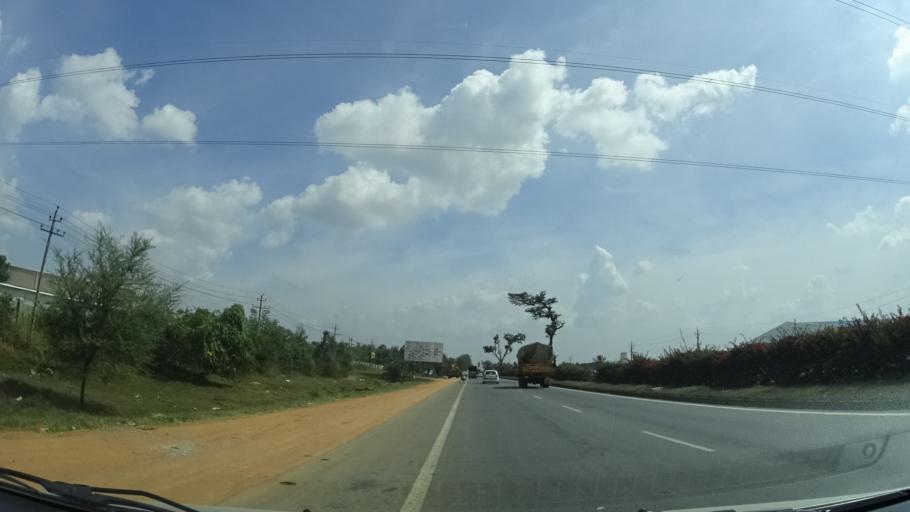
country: IN
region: Karnataka
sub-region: Bangalore Rural
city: Nelamangala
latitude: 13.1268
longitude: 77.3632
